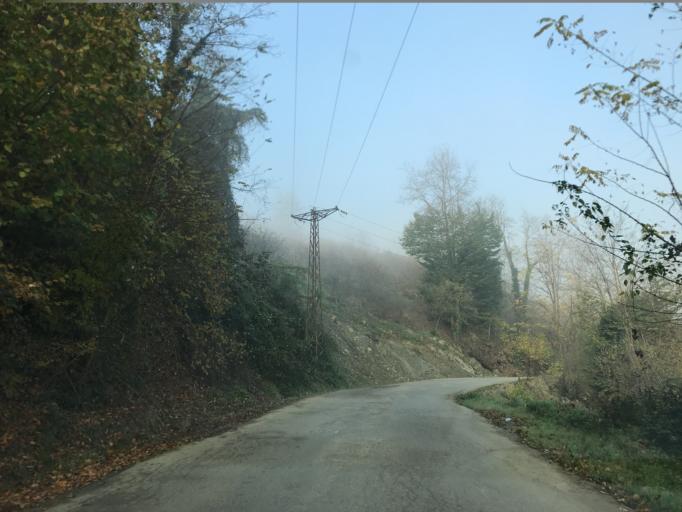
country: TR
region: Duzce
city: Cumayeri
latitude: 40.9148
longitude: 30.9364
